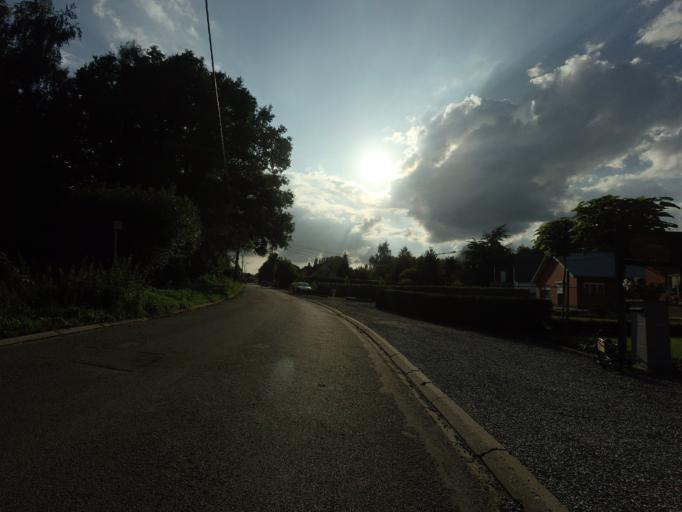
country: BE
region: Flanders
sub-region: Provincie Vlaams-Brabant
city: Boortmeerbeek
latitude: 50.9809
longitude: 4.5603
